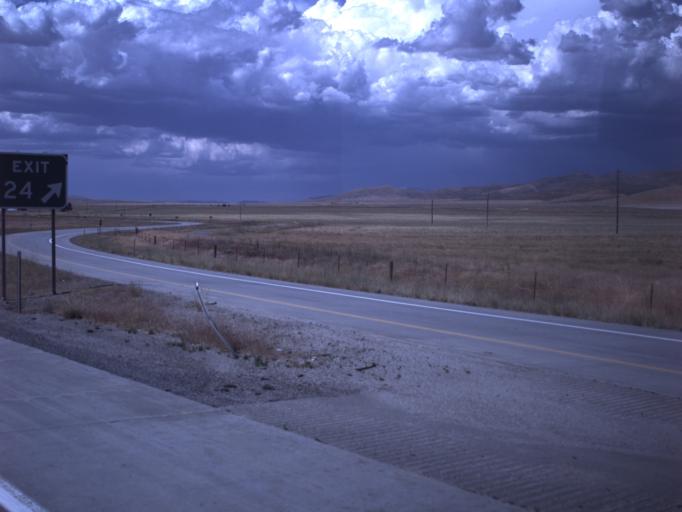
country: US
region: Utah
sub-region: Box Elder County
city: Garland
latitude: 41.8383
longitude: -112.4347
